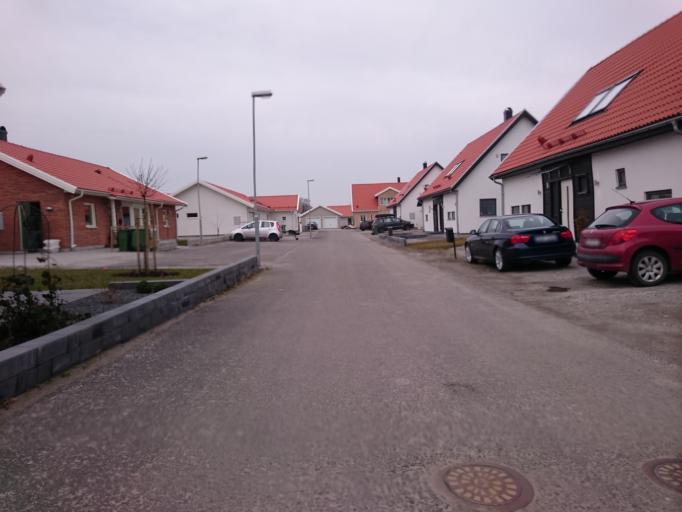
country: SE
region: Skane
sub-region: Lunds Kommun
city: Lund
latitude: 55.6781
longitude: 13.1759
